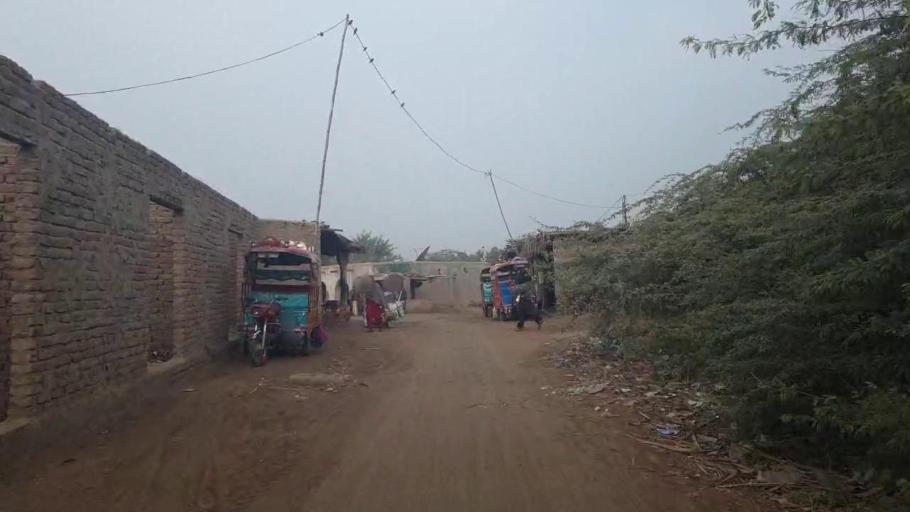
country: PK
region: Sindh
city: Tando Adam
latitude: 25.7109
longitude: 68.6469
